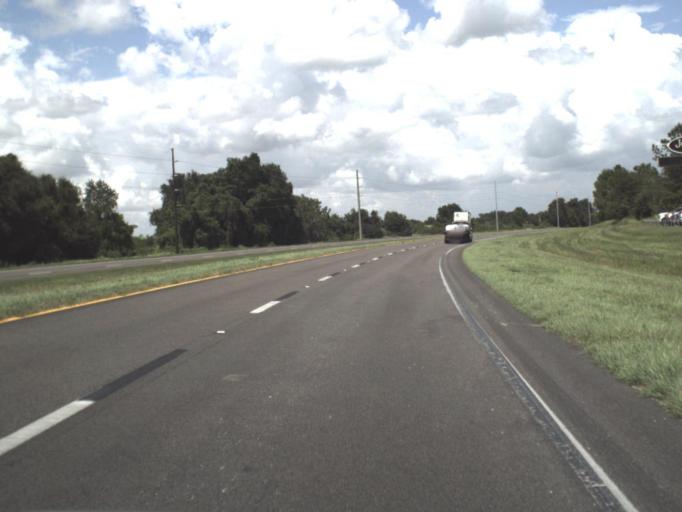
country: US
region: Florida
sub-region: Polk County
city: Fort Meade
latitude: 27.7890
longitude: -81.8131
